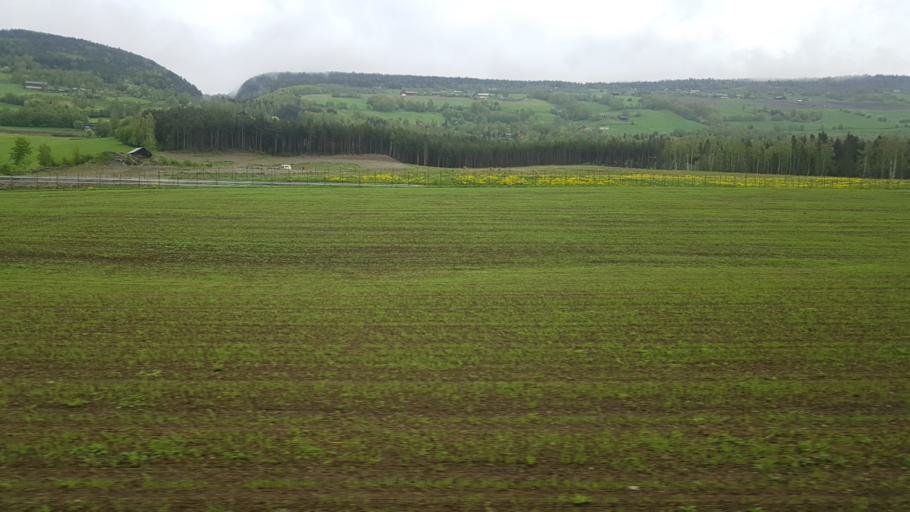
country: NO
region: Oppland
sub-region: Sor-Fron
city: Hundorp
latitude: 61.5688
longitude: 9.8742
